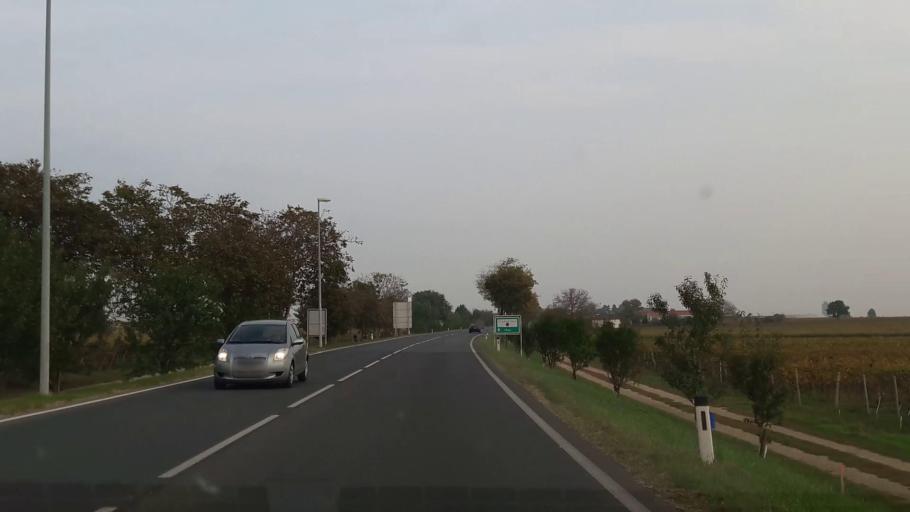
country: AT
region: Burgenland
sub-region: Politischer Bezirk Neusiedl am See
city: Weiden am See
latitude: 47.9116
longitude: 16.8893
